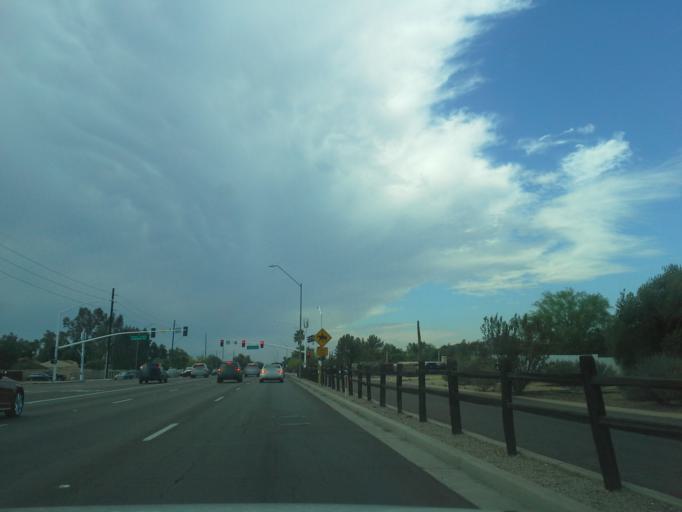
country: US
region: Arizona
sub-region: Maricopa County
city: Paradise Valley
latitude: 33.5978
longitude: -111.9261
